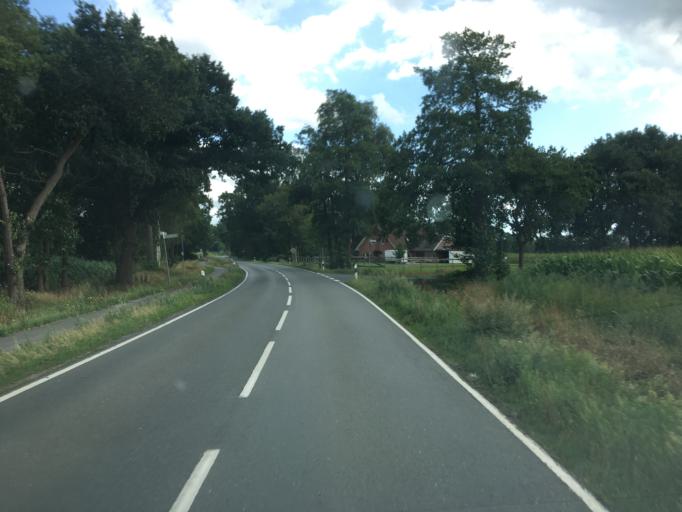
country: DE
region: Lower Saxony
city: Friesoythe
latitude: 53.0574
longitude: 7.8535
